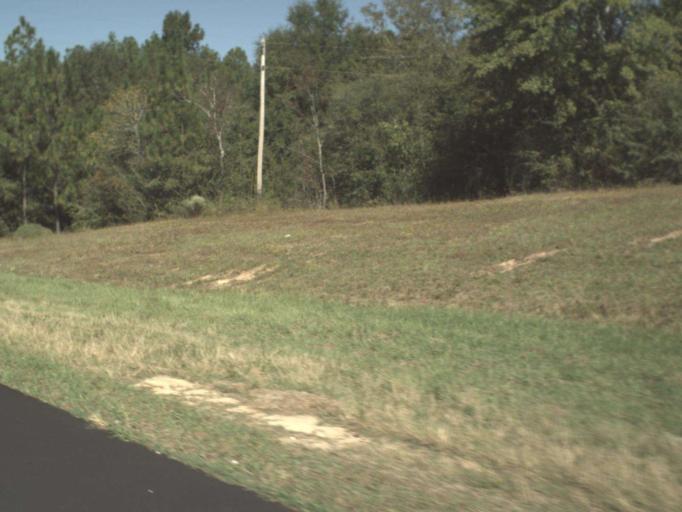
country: US
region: Florida
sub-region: Walton County
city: DeFuniak Springs
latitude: 30.8009
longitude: -86.1937
